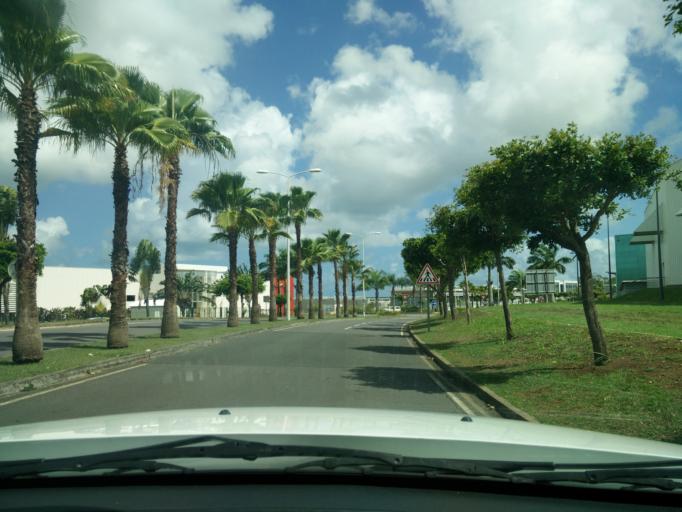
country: GP
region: Guadeloupe
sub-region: Guadeloupe
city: Les Abymes
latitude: 16.2669
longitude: -61.5174
